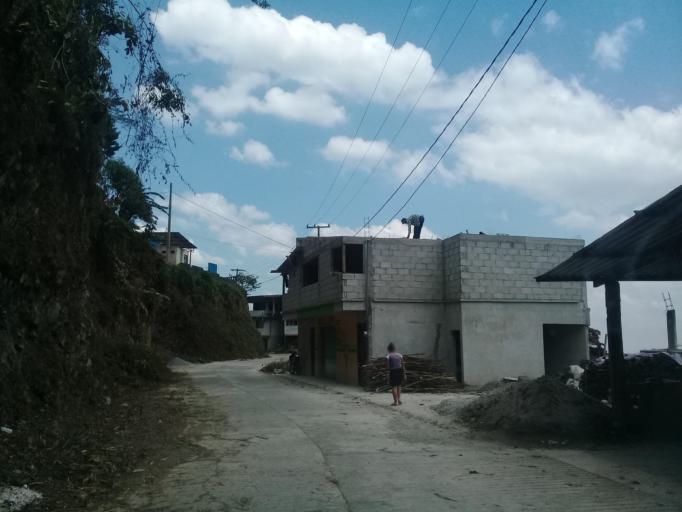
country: MX
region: Veracruz
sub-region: Tlilapan
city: Tonalixco
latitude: 18.7838
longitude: -97.0590
